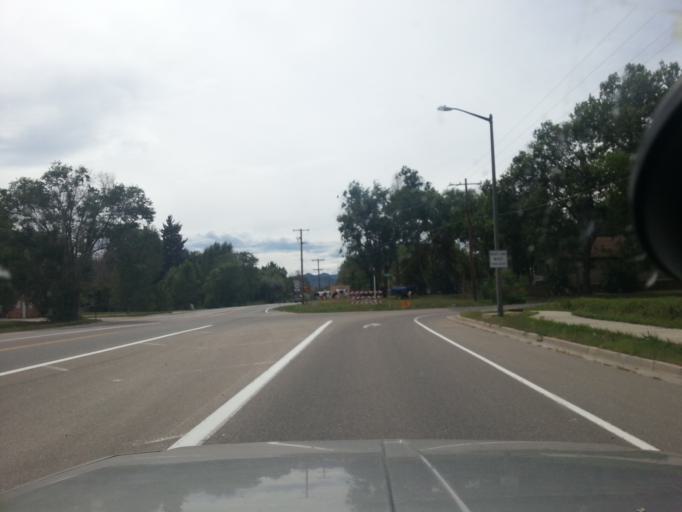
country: US
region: Colorado
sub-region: Larimer County
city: Loveland
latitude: 40.4074
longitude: -105.1337
